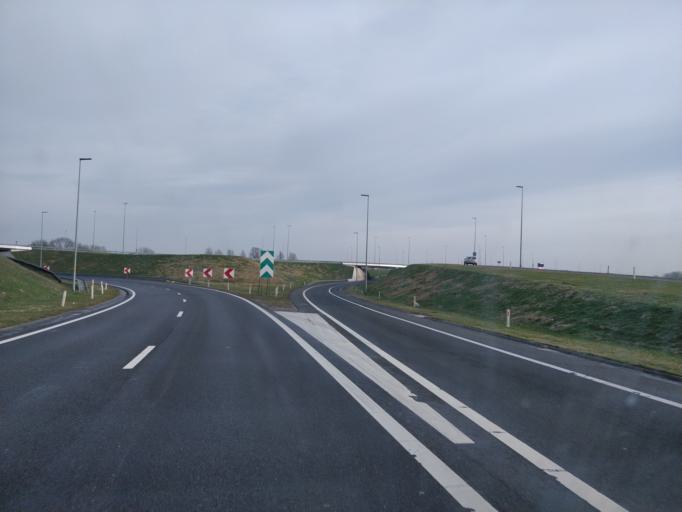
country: NL
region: Friesland
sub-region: Gemeente Leeuwarden
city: Wirdum
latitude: 53.1568
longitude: 5.7918
